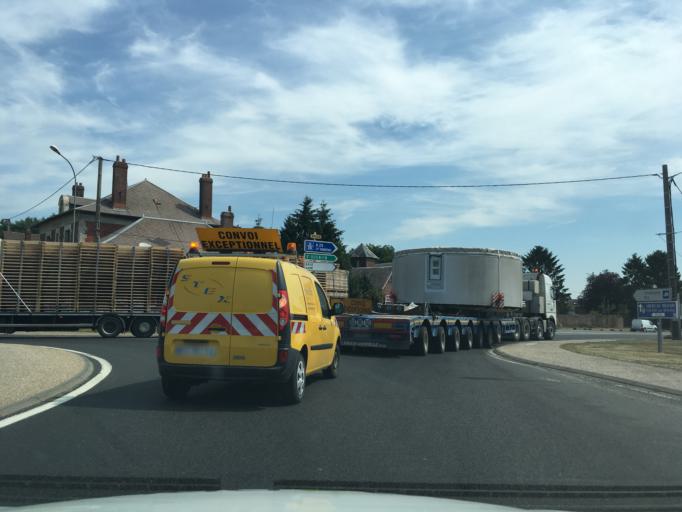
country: FR
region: Picardie
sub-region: Departement de la Somme
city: Peronne
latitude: 49.8765
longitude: 2.8955
